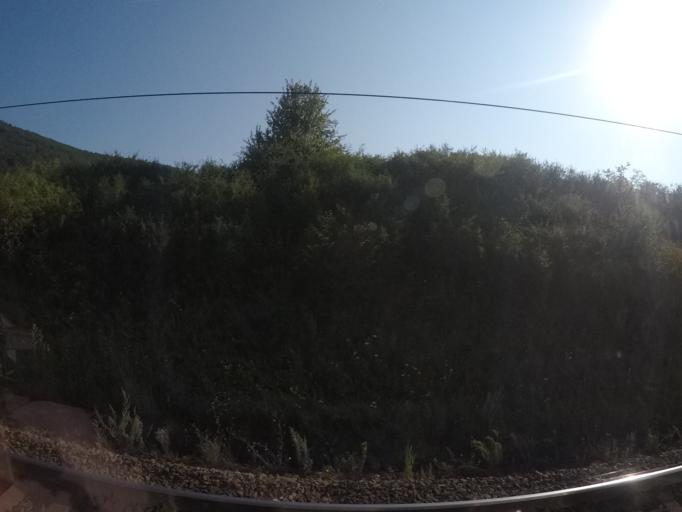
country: SK
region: Presovsky
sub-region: Okres Presov
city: Presov
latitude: 48.8601
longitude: 21.2213
